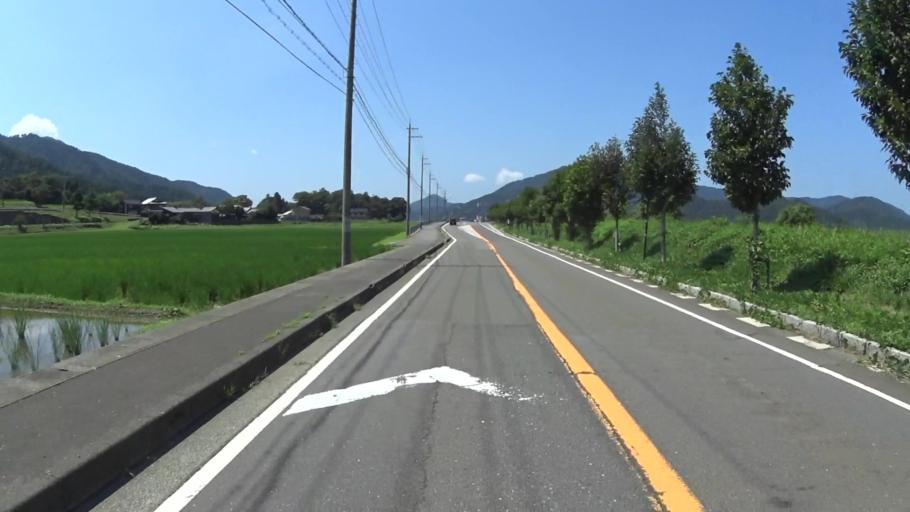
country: JP
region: Fukui
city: Obama
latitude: 35.4575
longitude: 135.8706
